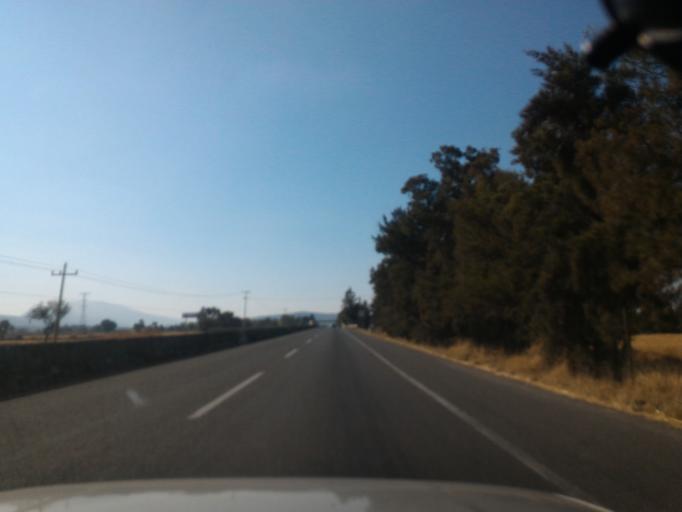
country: MX
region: Jalisco
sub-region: Ixtlahuacan de los Membrillos
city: Valle de los Girasoles [Fraccionamiento]
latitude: 20.4066
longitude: -103.1906
